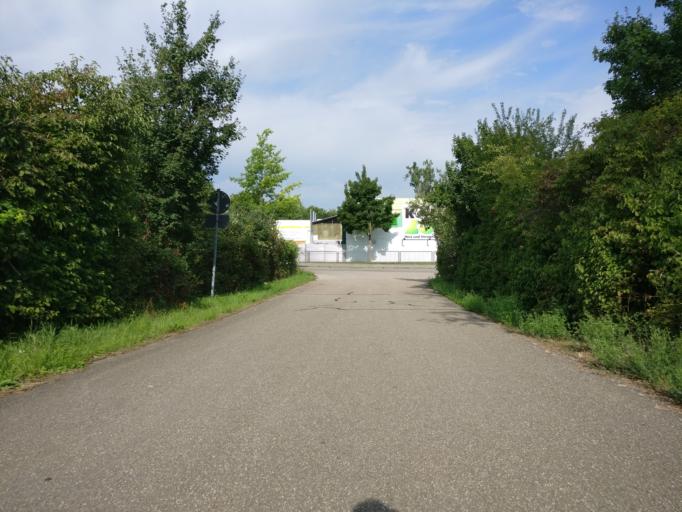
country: DE
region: Baden-Wuerttemberg
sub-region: Karlsruhe Region
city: Karlsruhe
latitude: 49.0183
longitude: 8.4673
